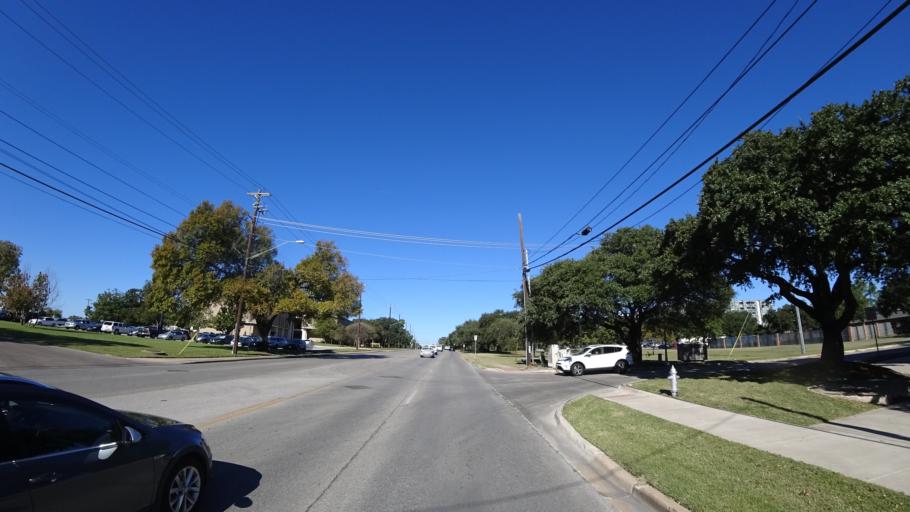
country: US
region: Texas
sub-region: Travis County
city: Austin
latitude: 30.3122
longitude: -97.7352
